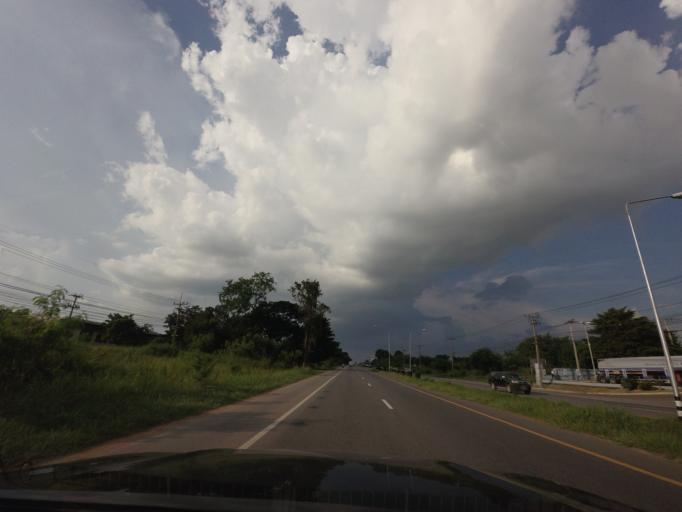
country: TH
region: Khon Kaen
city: Ban Haet
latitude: 16.3097
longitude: 102.7911
